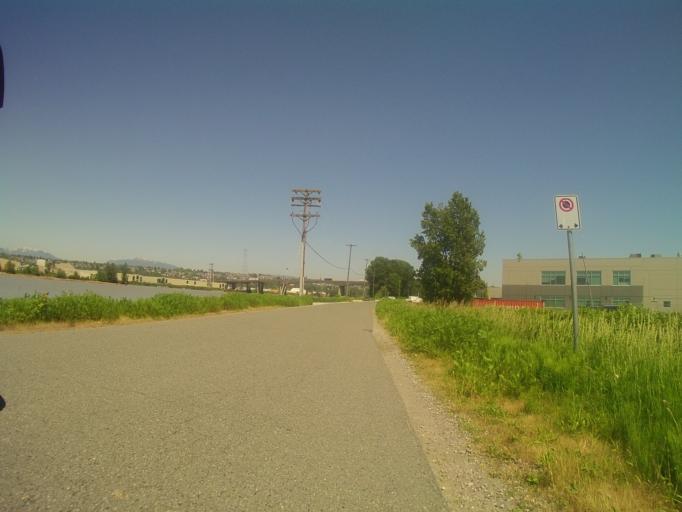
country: CA
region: British Columbia
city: Richmond
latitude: 49.1985
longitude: -123.0836
